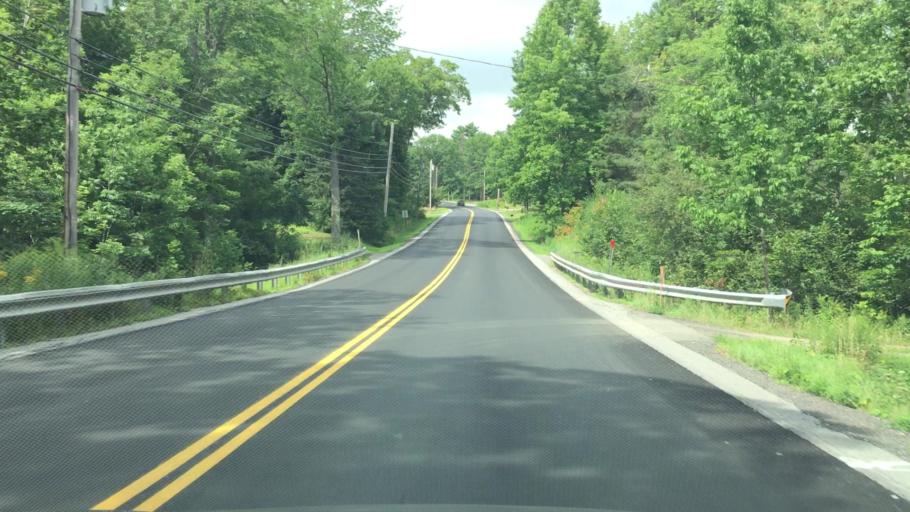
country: US
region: Maine
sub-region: Hancock County
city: Bucksport
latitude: 44.6017
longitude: -68.8161
